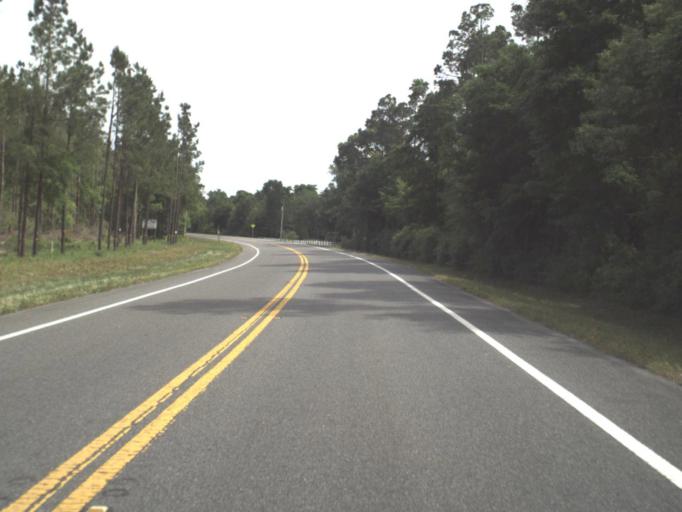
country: US
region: Florida
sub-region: Santa Rosa County
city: Point Baker
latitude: 30.7360
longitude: -87.0933
